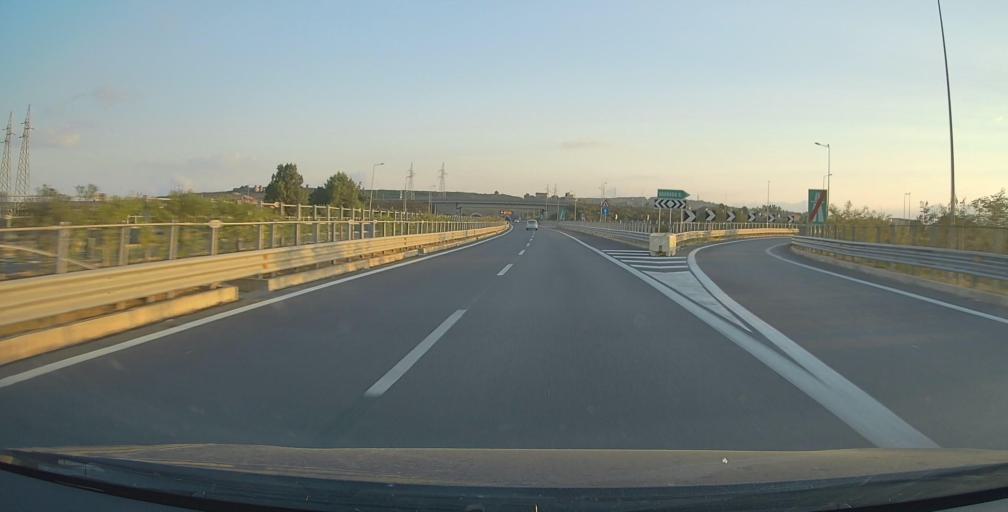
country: IT
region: Calabria
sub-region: Provincia di Reggio Calabria
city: Ceramida-Pellegrina
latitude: 38.3099
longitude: 15.8445
